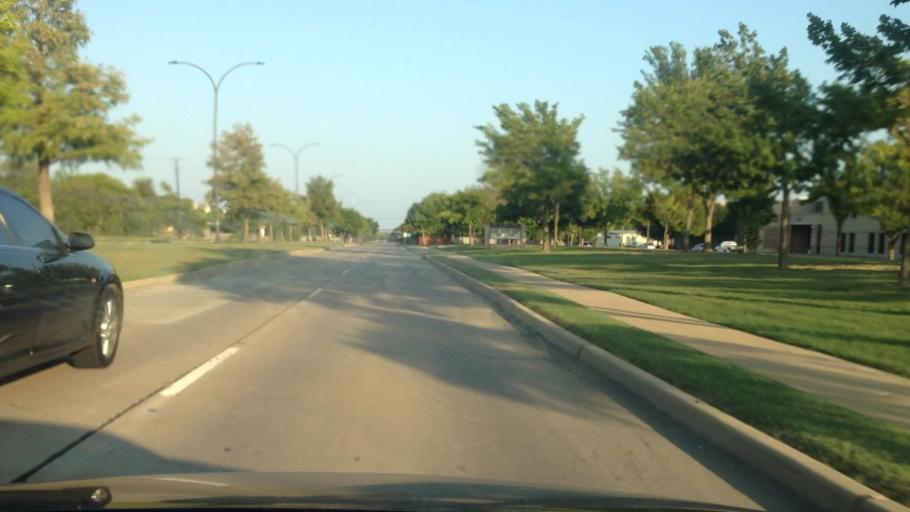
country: US
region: Texas
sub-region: Tarrant County
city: Dalworthington Gardens
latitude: 32.6566
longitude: -97.1047
